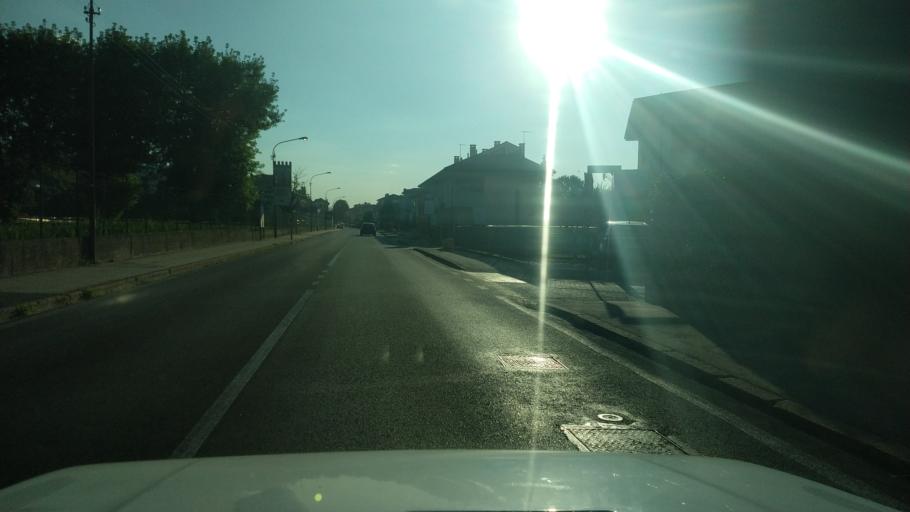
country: IT
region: Veneto
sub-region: Provincia di Vicenza
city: Marostica
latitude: 45.7424
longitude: 11.6508
